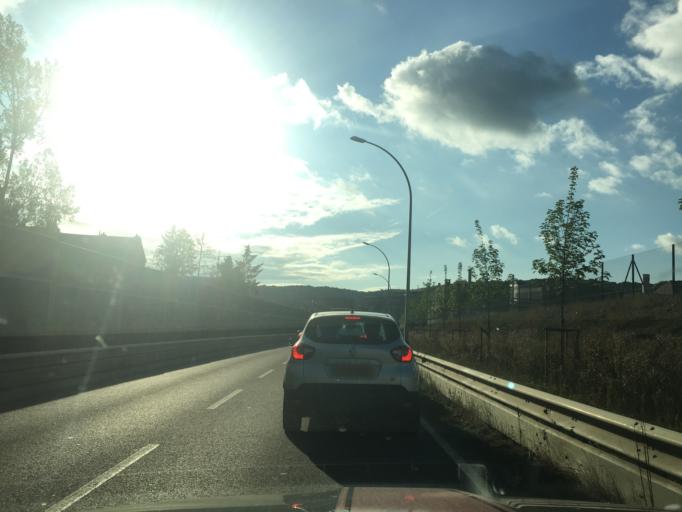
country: LU
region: Luxembourg
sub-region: Canton d'Esch-sur-Alzette
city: Obercorn
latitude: 49.5228
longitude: 5.9049
